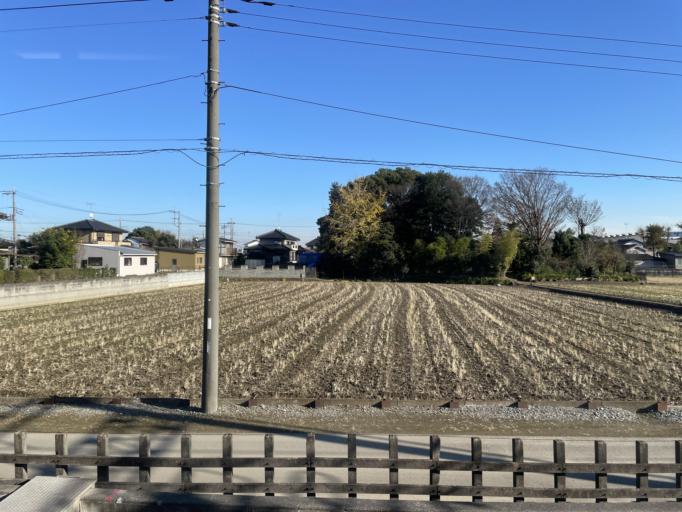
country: JP
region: Saitama
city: Satte
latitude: 36.1011
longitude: 139.7206
